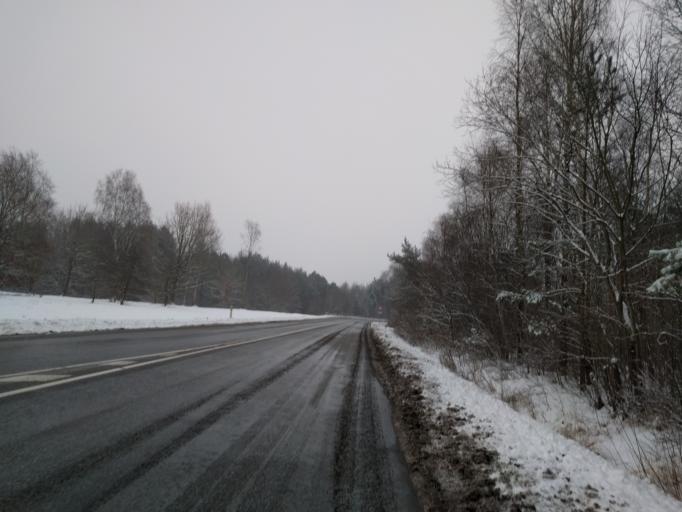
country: DK
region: Central Jutland
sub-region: Viborg Kommune
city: Viborg
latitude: 56.4239
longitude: 9.3991
